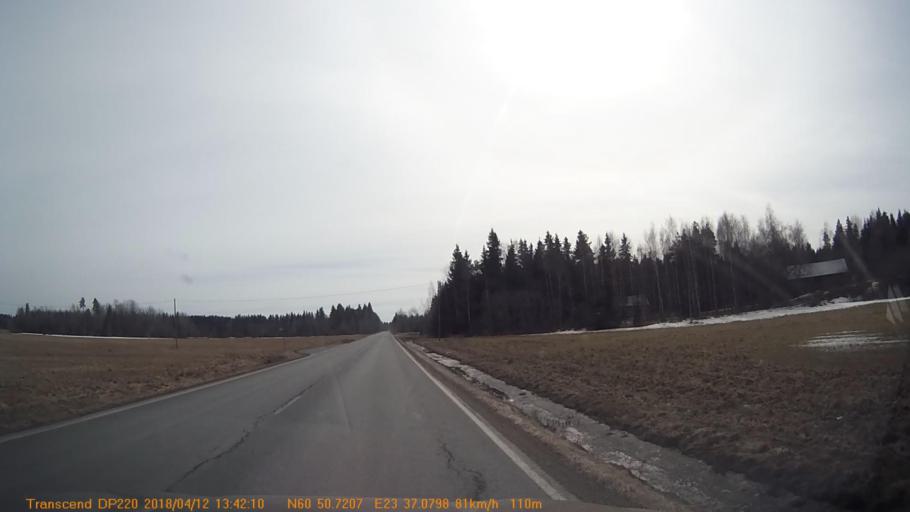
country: FI
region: Haeme
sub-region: Forssa
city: Forssa
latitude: 60.8447
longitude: 23.6180
